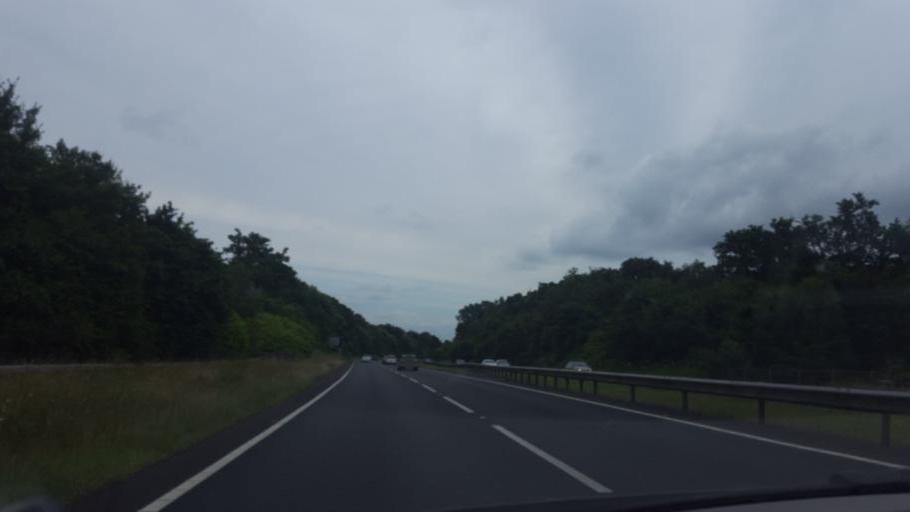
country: GB
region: England
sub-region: Royal Borough of Windsor and Maidenhead
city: Bisham
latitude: 51.5250
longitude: -0.7771
